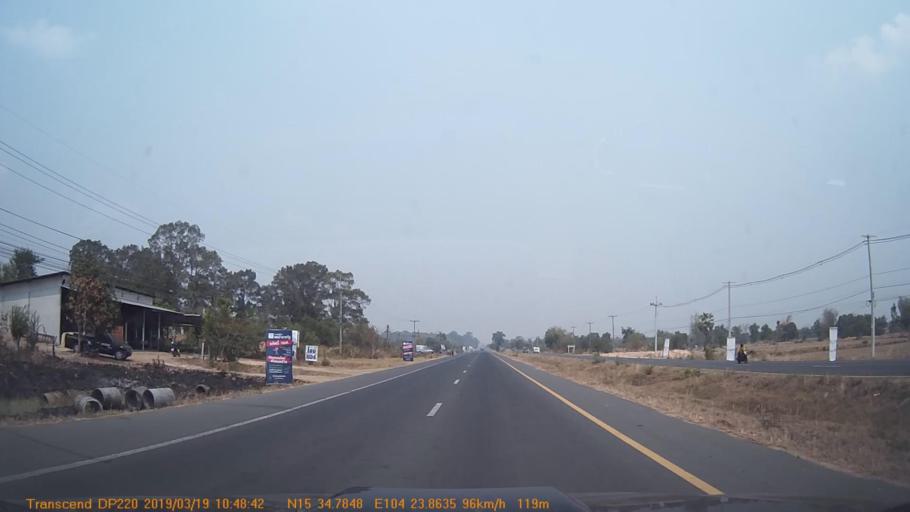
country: TH
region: Yasothon
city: Kham Khuean Kaeo
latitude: 15.5799
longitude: 104.3976
